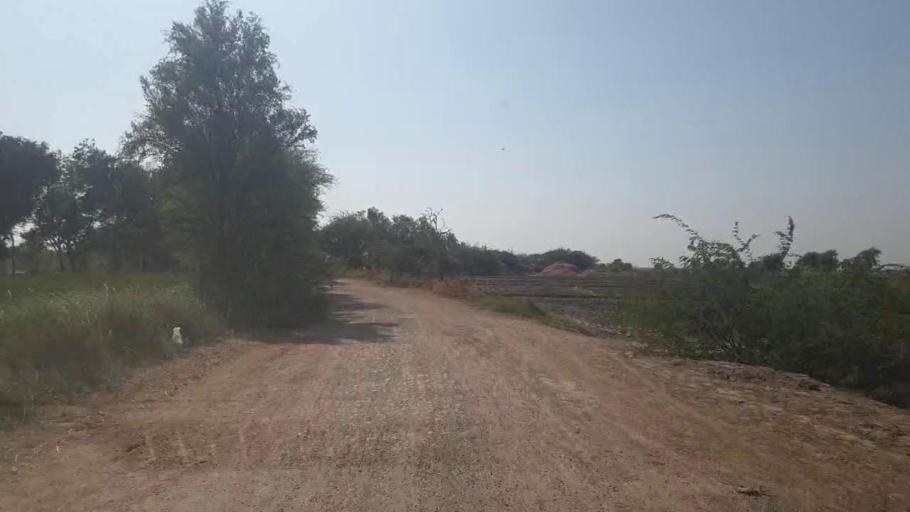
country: PK
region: Sindh
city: Badin
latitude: 24.5500
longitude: 68.8459
